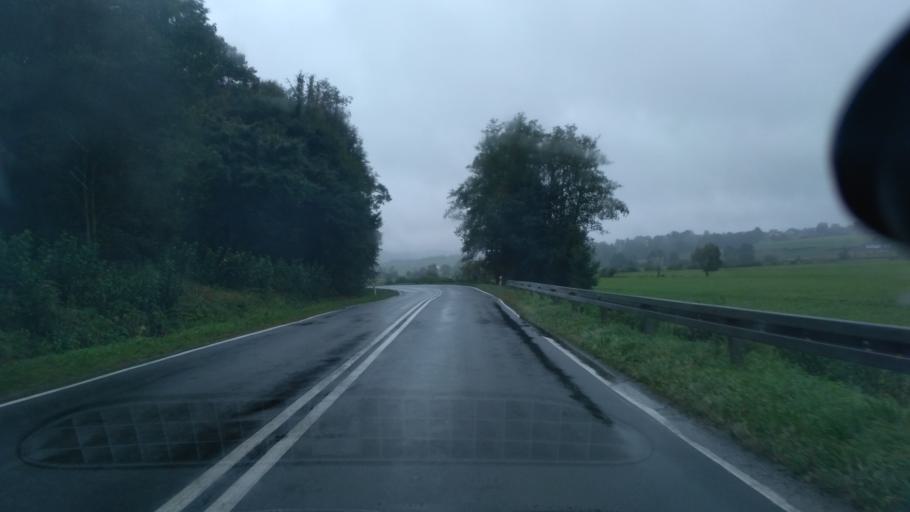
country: PL
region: Subcarpathian Voivodeship
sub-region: Powiat ropczycko-sedziszowski
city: Niedzwiada
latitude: 49.9904
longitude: 21.5631
